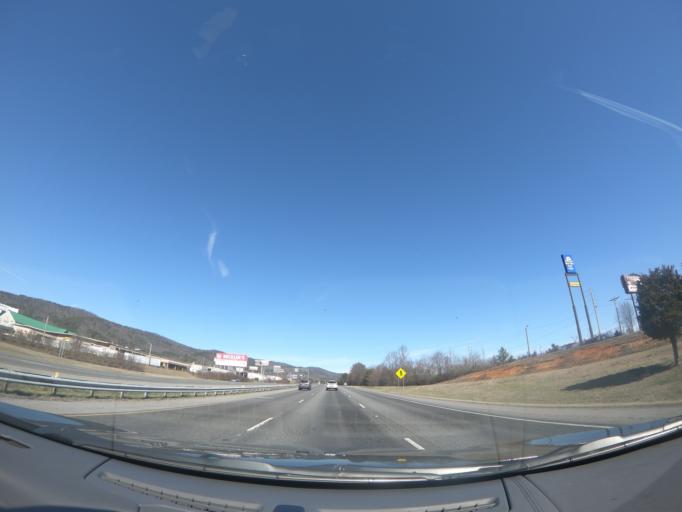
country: US
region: Georgia
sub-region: Whitfield County
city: Dalton
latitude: 34.6887
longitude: -85.0021
